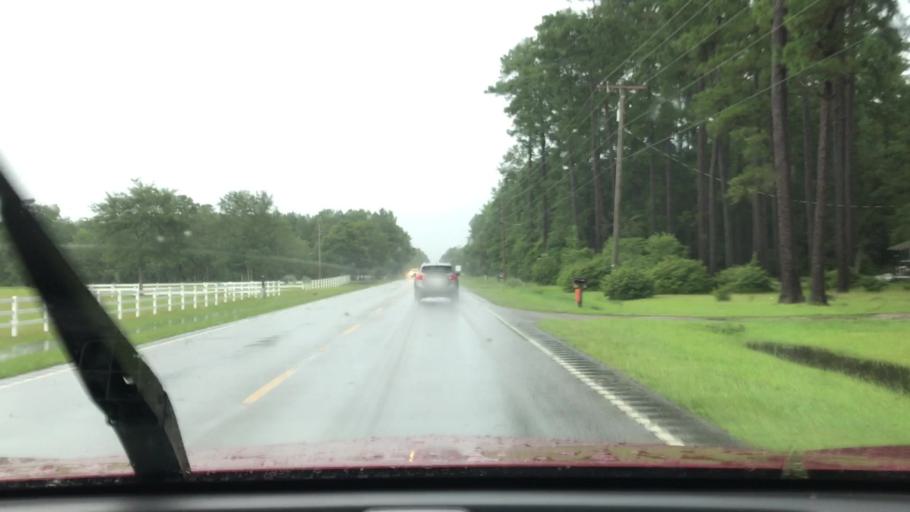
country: US
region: South Carolina
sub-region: Horry County
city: Conway
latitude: 33.7438
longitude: -79.0796
